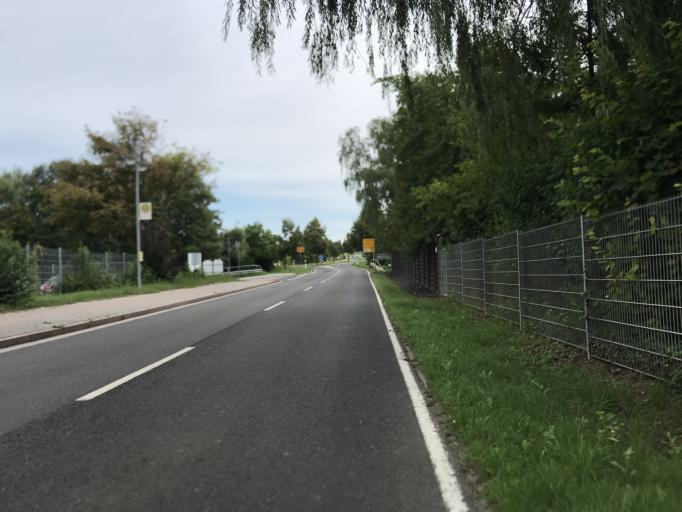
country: DE
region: Rheinland-Pfalz
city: Sprendlingen
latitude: 49.8641
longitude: 7.9924
